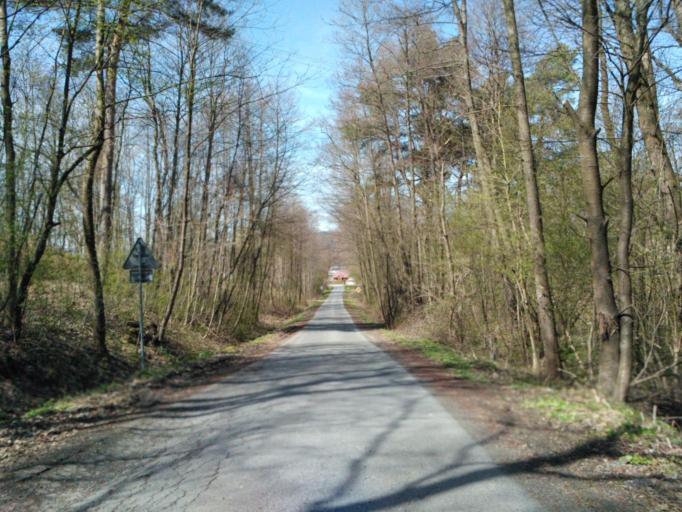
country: PL
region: Subcarpathian Voivodeship
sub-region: Powiat strzyzowski
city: Babica
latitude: 49.9256
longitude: 21.8868
